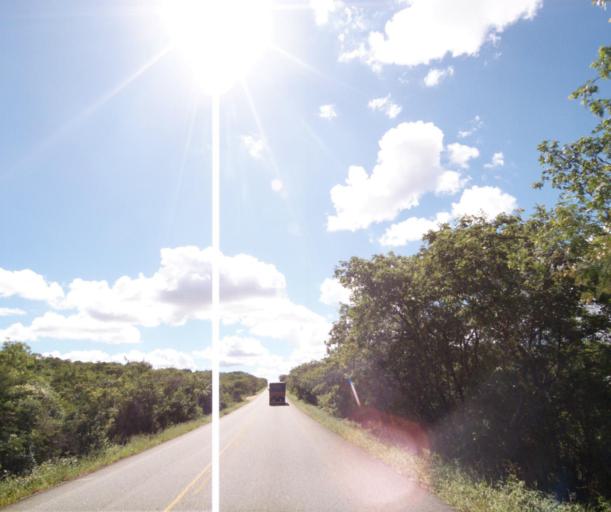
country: BR
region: Bahia
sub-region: Caetite
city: Caetite
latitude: -14.1719
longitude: -42.2065
